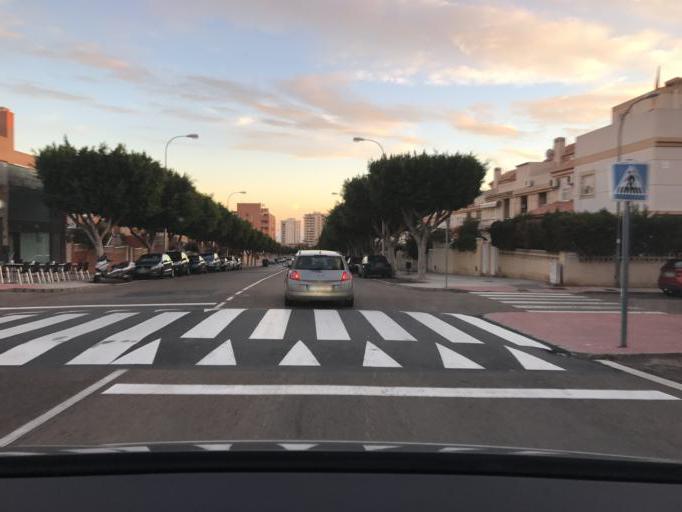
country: ES
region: Andalusia
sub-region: Provincia de Almeria
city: Aguadulce
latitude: 36.8161
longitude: -2.5803
